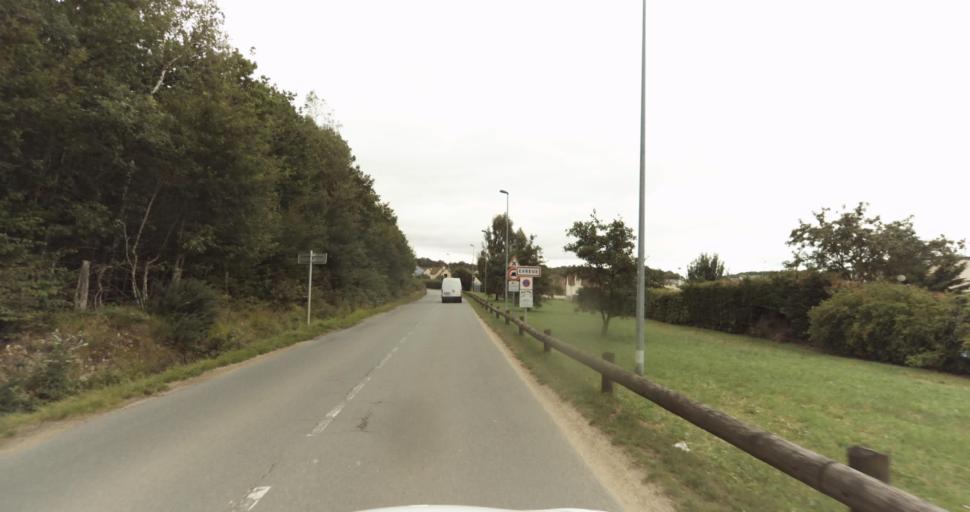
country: FR
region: Haute-Normandie
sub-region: Departement de l'Eure
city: Gravigny
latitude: 49.0366
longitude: 1.1739
